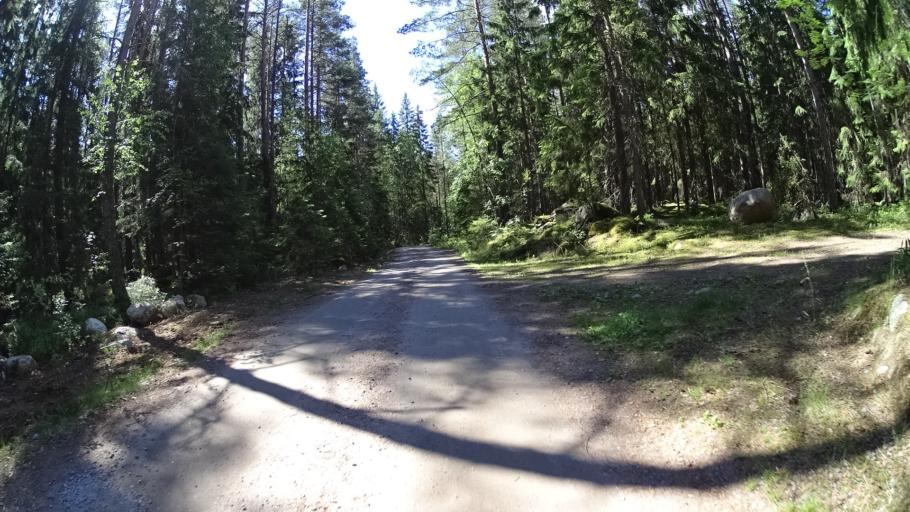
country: FI
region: Uusimaa
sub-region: Helsinki
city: Vihti
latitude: 60.3152
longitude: 24.4467
